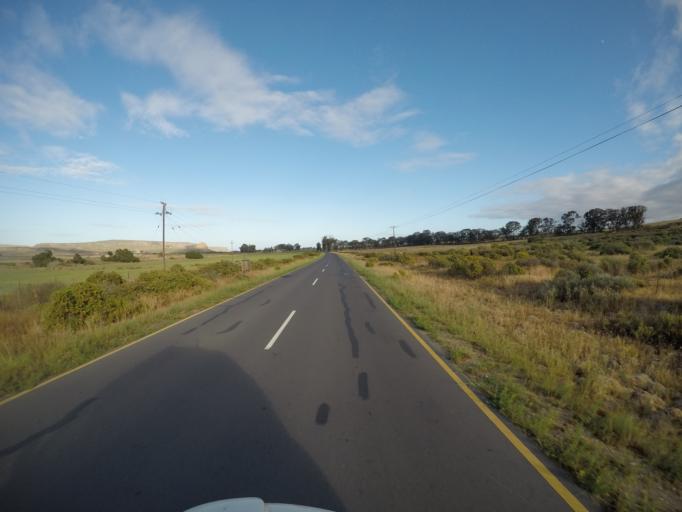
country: ZA
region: Western Cape
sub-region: West Coast District Municipality
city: Clanwilliam
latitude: -32.3125
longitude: 18.3883
